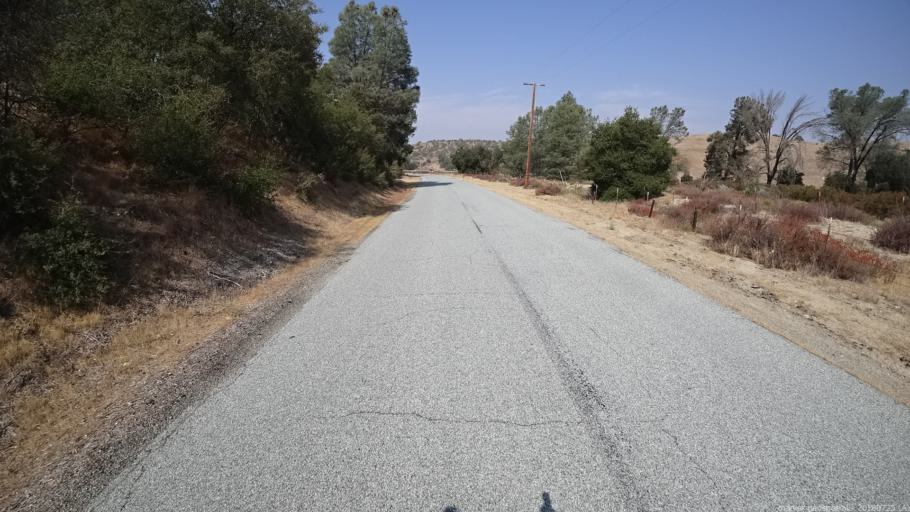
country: US
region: California
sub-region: San Luis Obispo County
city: San Miguel
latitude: 35.8564
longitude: -120.5995
